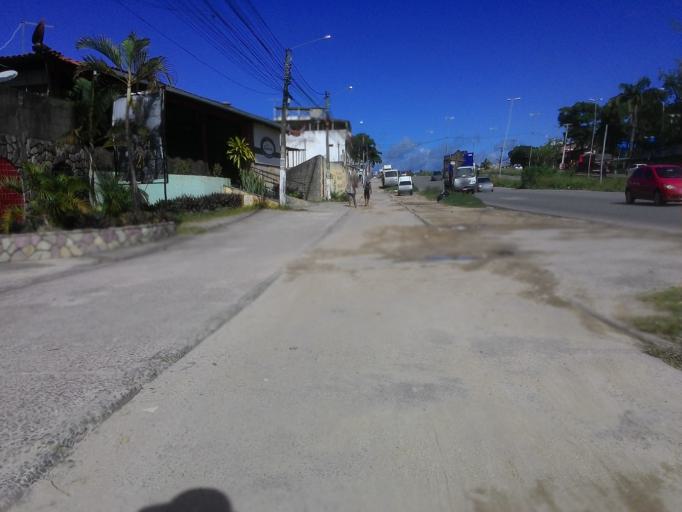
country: BR
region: Pernambuco
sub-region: Olinda
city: Olinda
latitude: -7.9792
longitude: -34.8594
